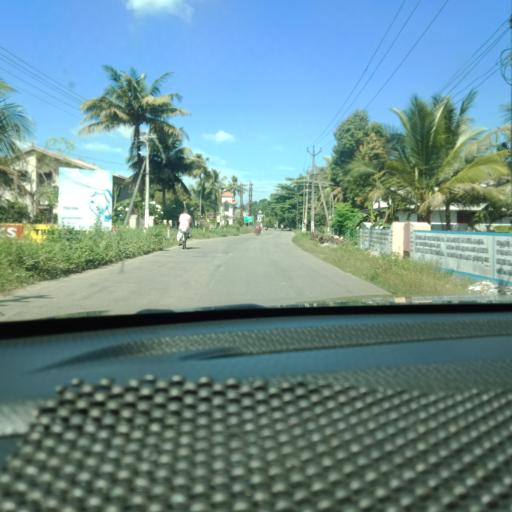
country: IN
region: Kerala
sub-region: Alappuzha
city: Mavelikara
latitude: 9.3076
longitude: 76.4567
